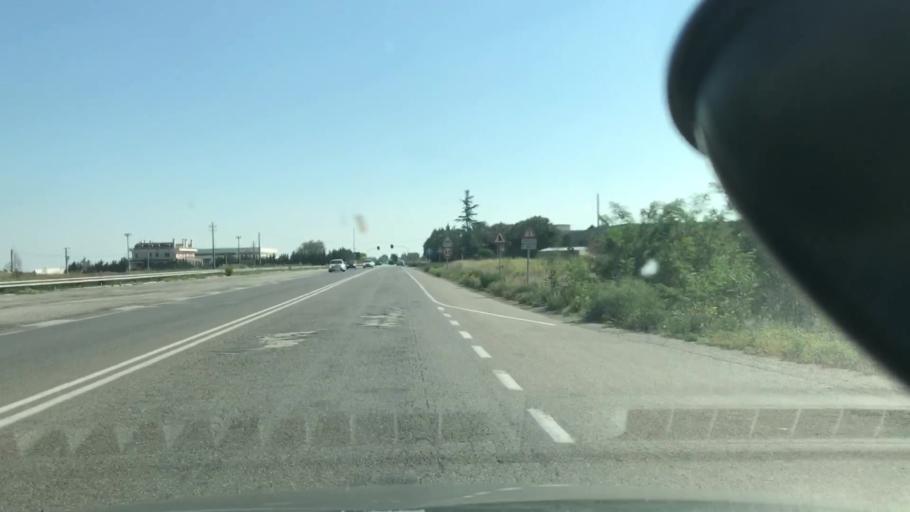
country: IT
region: Apulia
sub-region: Provincia di Foggia
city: Foggia
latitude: 41.4264
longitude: 15.5635
